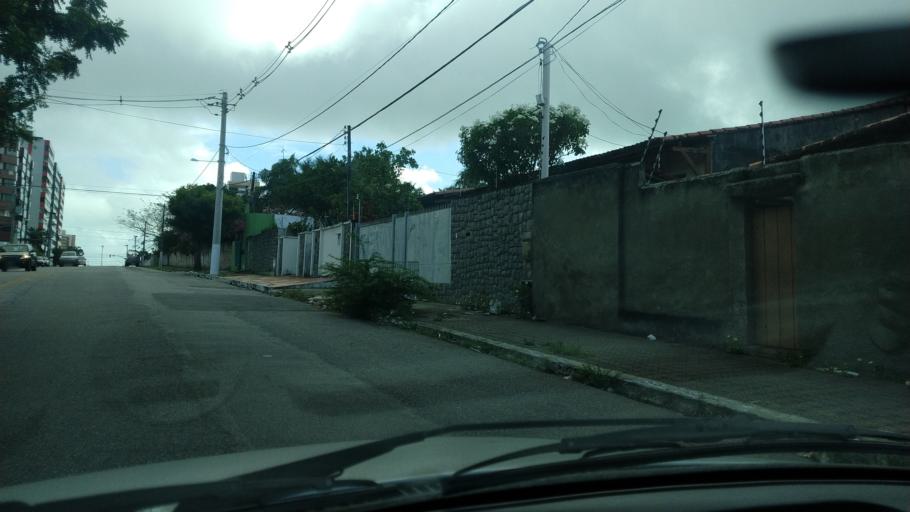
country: BR
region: Rio Grande do Norte
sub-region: Natal
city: Natal
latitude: -5.8153
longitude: -35.2202
